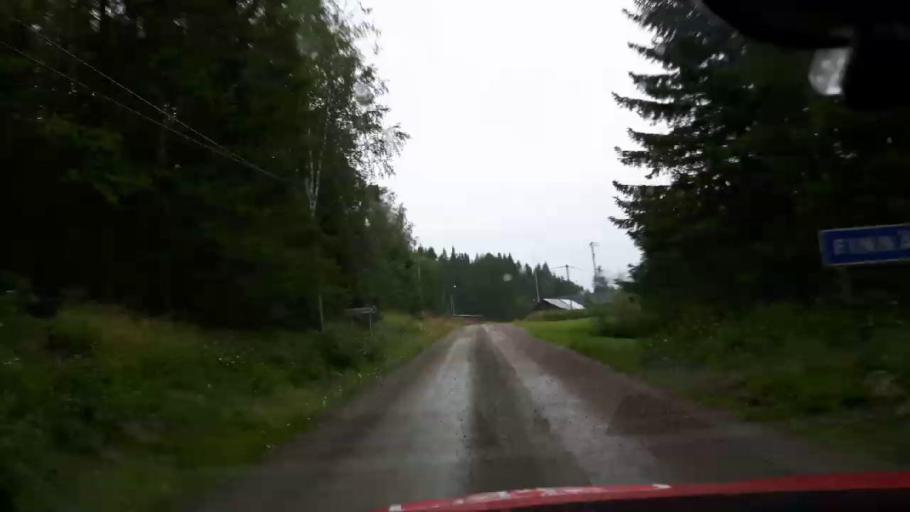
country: SE
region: Jaemtland
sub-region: OEstersunds Kommun
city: Brunflo
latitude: 62.7839
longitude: 14.9697
